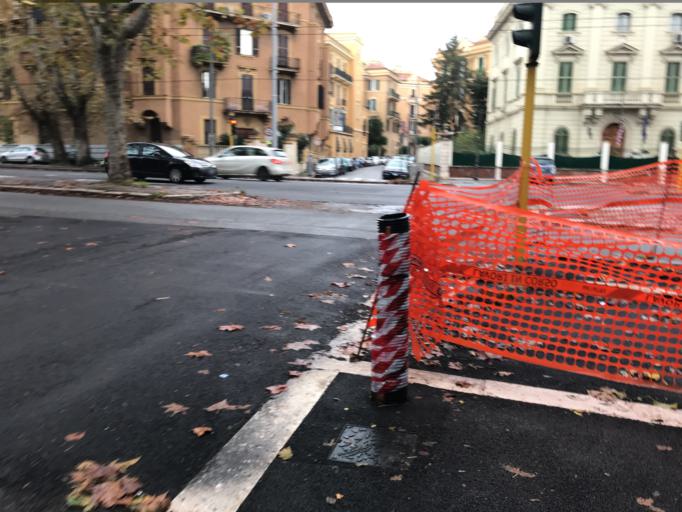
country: IT
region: Latium
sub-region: Citta metropolitana di Roma Capitale
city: Rome
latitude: 41.9166
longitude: 12.5124
